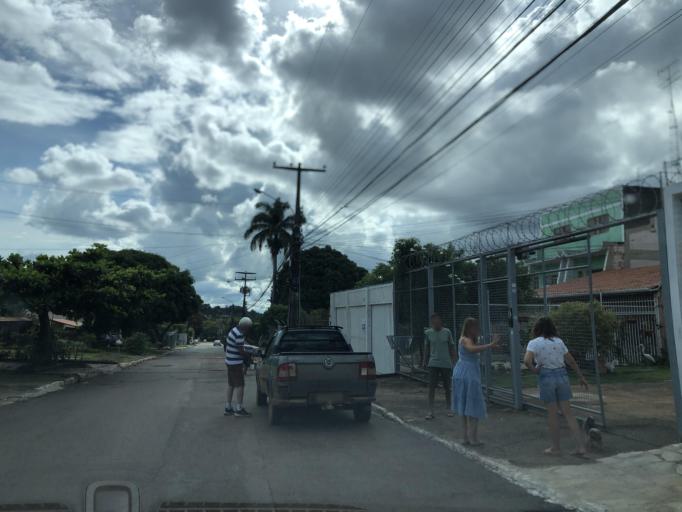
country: BR
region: Federal District
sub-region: Brasilia
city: Brasilia
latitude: -15.8393
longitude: -48.0614
